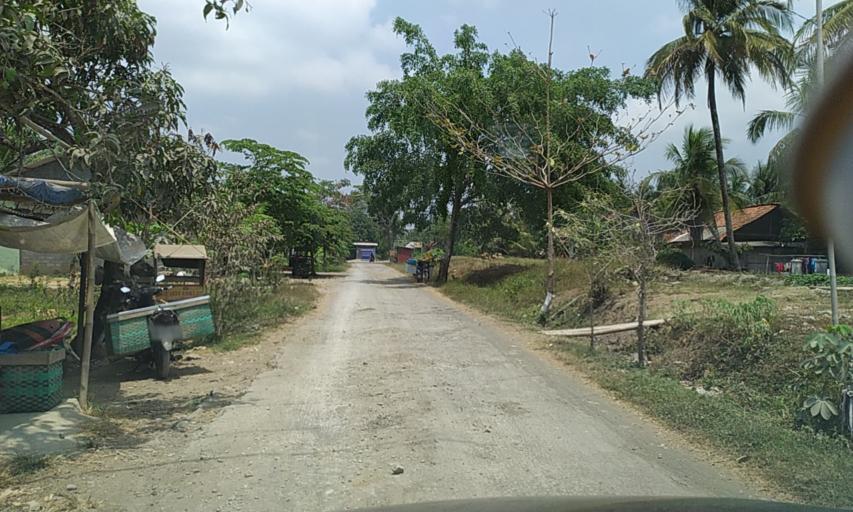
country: ID
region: Central Java
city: Sidakaya
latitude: -7.5784
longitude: 108.8621
